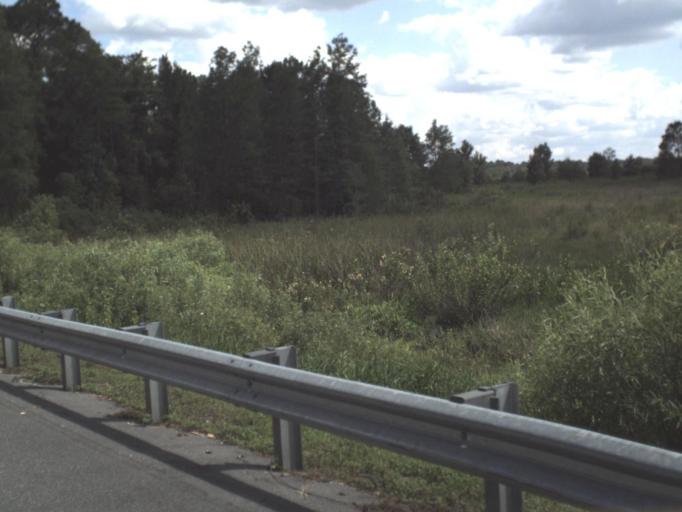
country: US
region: Florida
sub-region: Clay County
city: Keystone Heights
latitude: 29.7371
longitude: -81.9608
